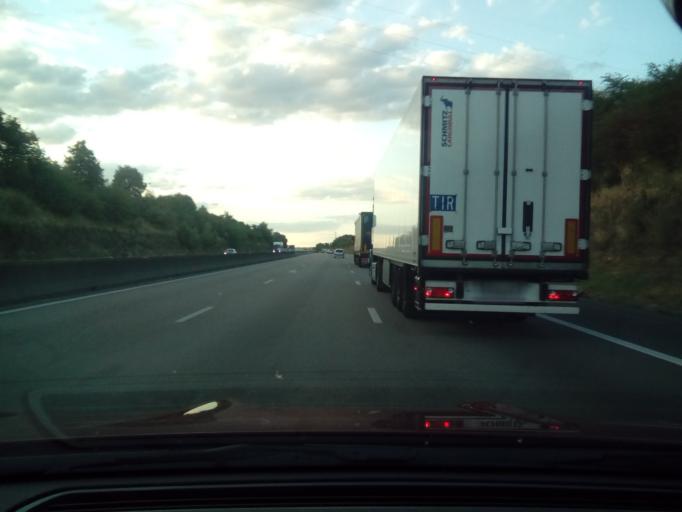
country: FR
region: Rhone-Alpes
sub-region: Departement de l'Isere
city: Chanas
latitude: 45.3286
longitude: 4.8117
